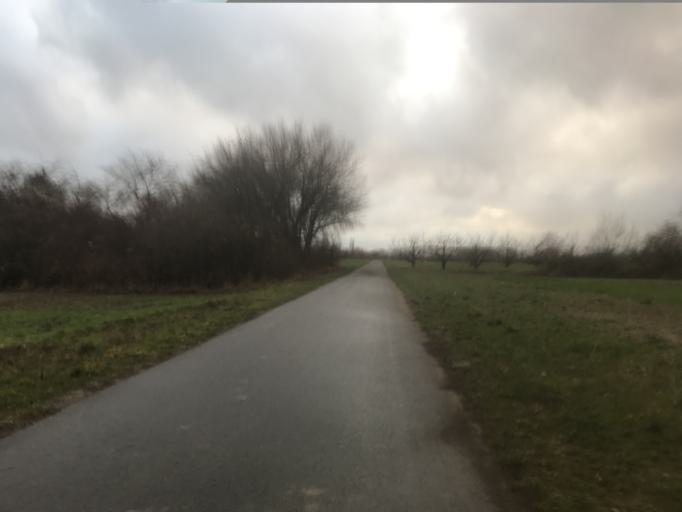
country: DE
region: Hesse
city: Geisenheim
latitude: 49.9764
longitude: 7.9918
